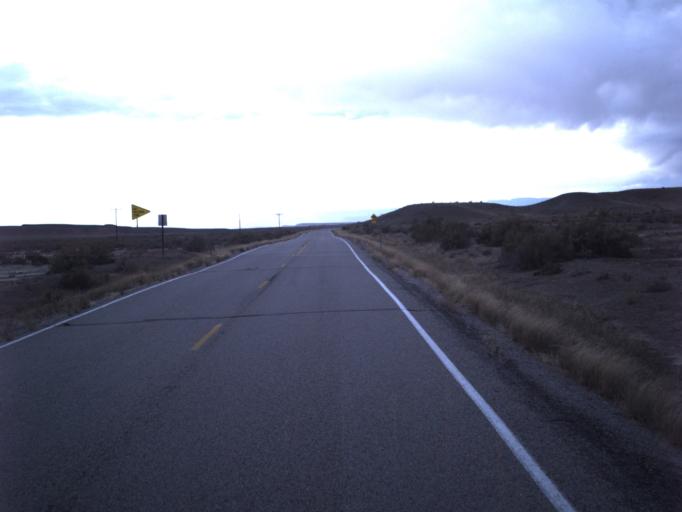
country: US
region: Utah
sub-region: Grand County
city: Moab
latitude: 38.8693
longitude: -109.2984
